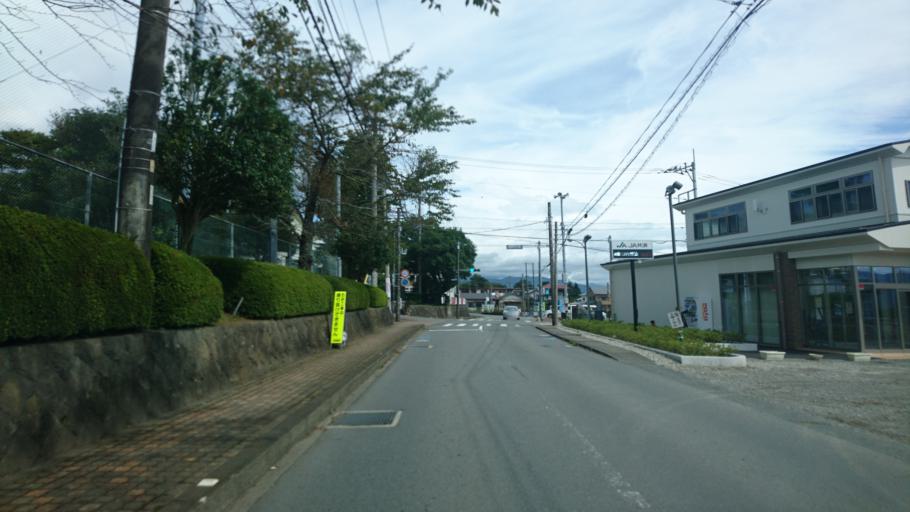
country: JP
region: Shizuoka
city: Gotemba
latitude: 35.3154
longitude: 138.9063
